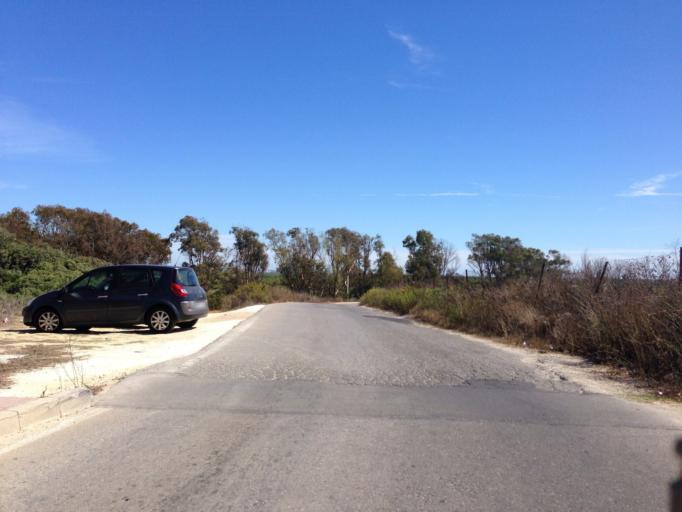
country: ES
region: Andalusia
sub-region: Provincia de Cadiz
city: Chiclana de la Frontera
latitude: 36.3337
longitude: -6.1567
